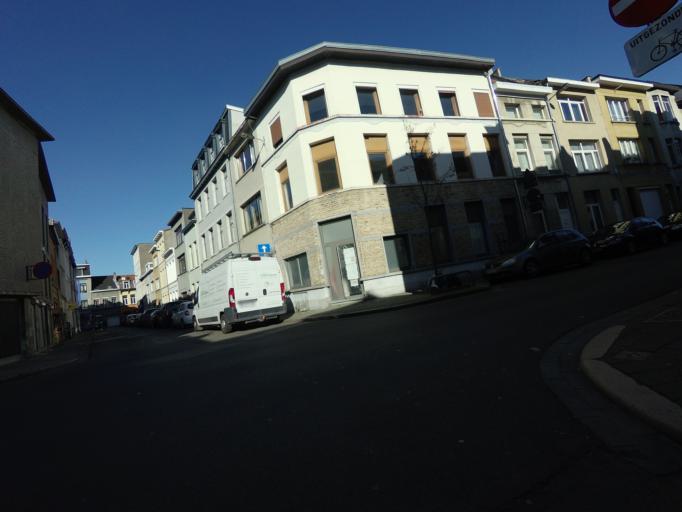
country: BE
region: Flanders
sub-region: Provincie Antwerpen
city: Antwerpen
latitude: 51.2209
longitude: 4.4326
